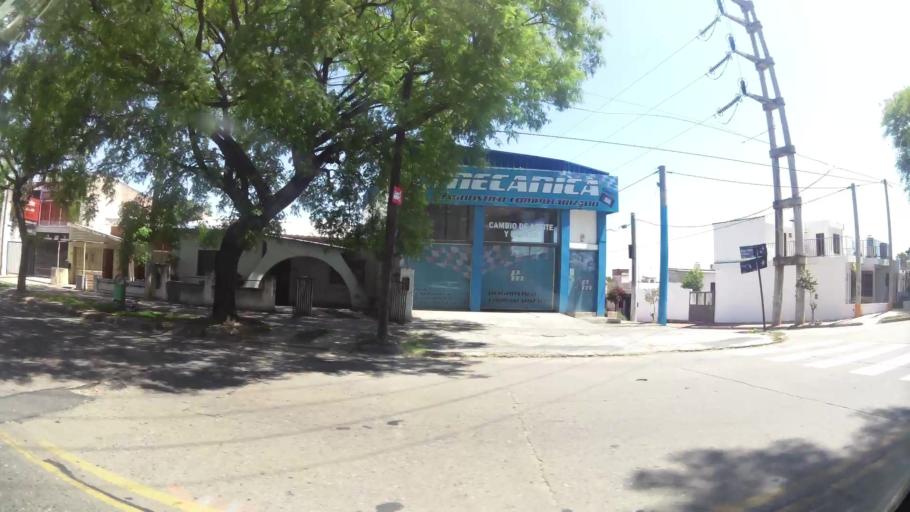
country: AR
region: Cordoba
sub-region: Departamento de Capital
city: Cordoba
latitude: -31.3867
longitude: -64.2047
